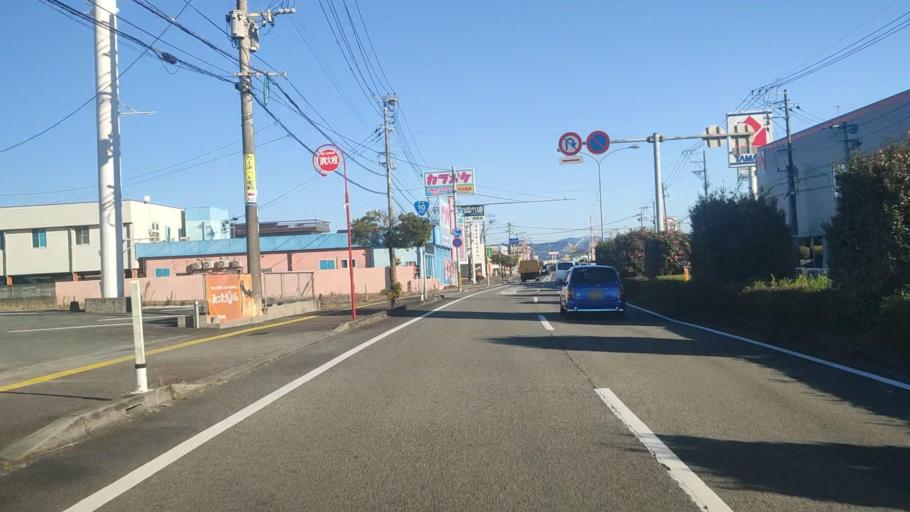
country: JP
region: Miyazaki
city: Nobeoka
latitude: 32.5500
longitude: 131.6772
